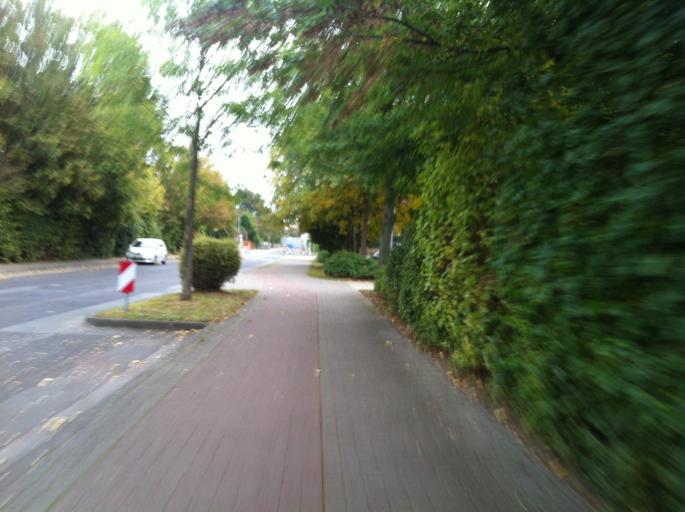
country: DE
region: Rheinland-Pfalz
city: Klein-Winternheim
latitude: 49.9722
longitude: 8.2329
